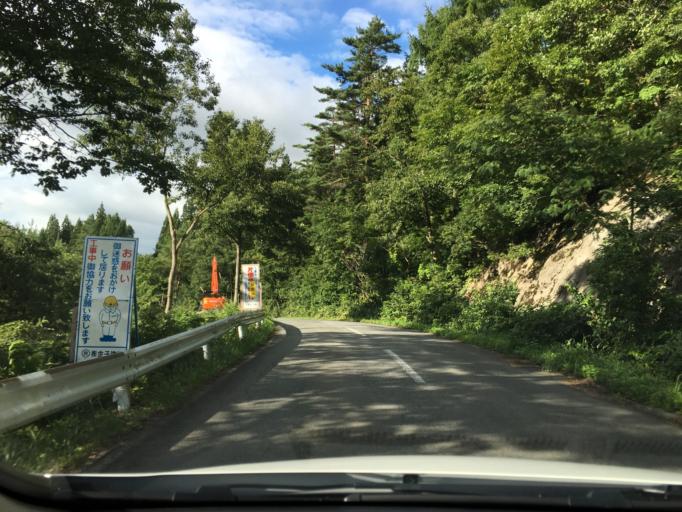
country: JP
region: Yamagata
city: Yonezawa
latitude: 37.9077
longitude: 140.2049
